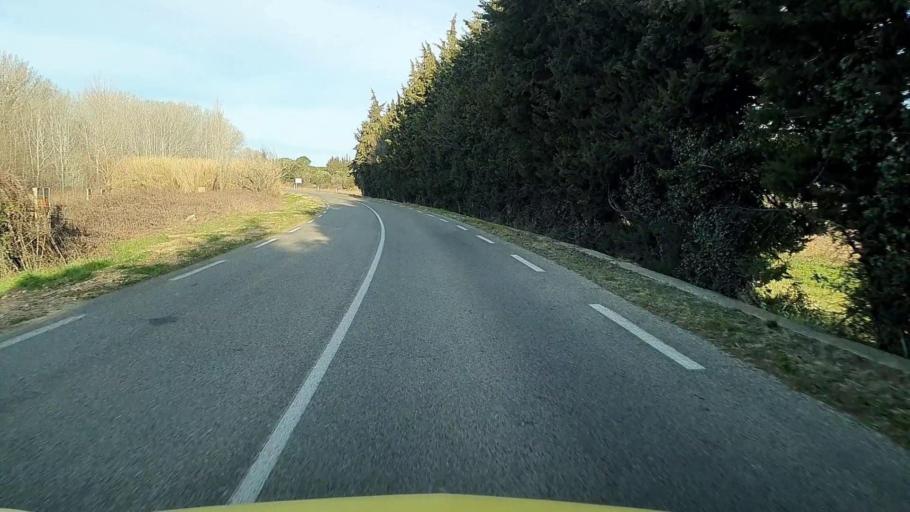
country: FR
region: Languedoc-Roussillon
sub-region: Departement du Gard
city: Castillon-du-Gard
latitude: 43.9508
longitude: 4.5578
